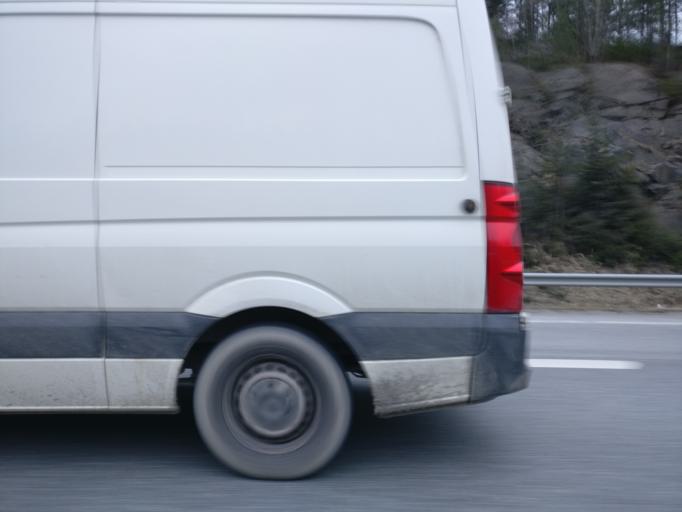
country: FI
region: Haeme
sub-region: Haemeenlinna
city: Tervakoski
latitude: 60.8187
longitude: 24.6715
